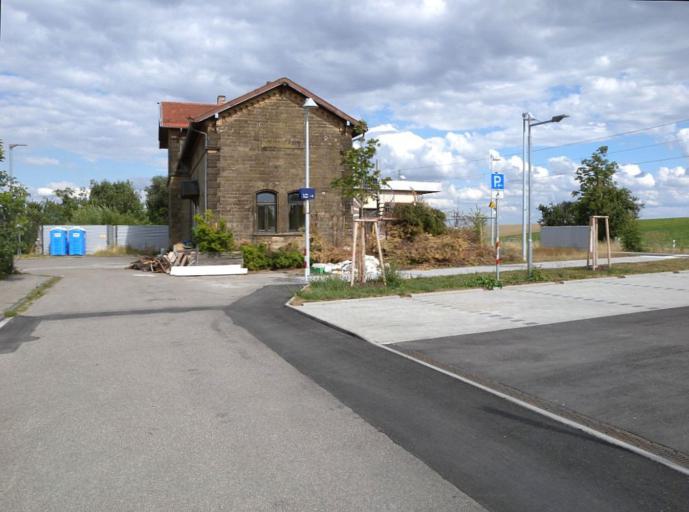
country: DE
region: Baden-Wuerttemberg
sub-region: Regierungsbezirk Stuttgart
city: Kirchardt
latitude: 49.2264
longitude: 8.9972
